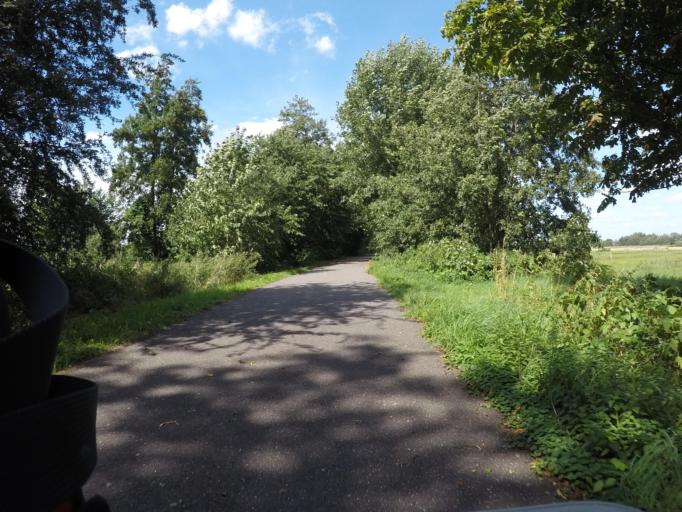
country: DE
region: Lower Saxony
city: Stelle
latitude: 53.4331
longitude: 10.1424
